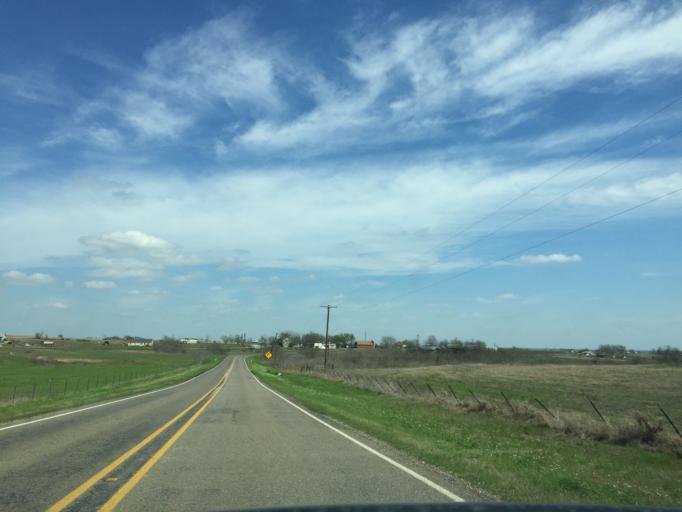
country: US
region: Texas
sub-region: Williamson County
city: Taylor
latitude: 30.5573
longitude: -97.3092
